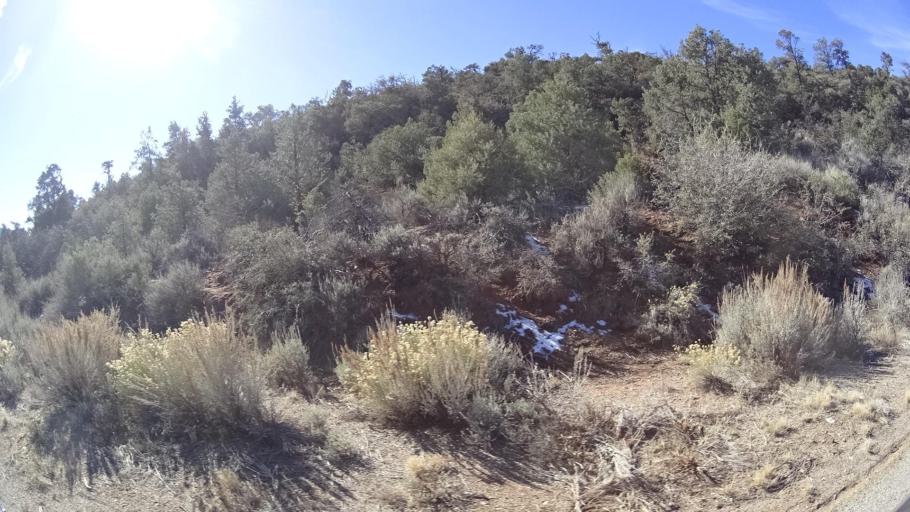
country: US
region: California
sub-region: Kern County
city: Pine Mountain Club
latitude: 34.8676
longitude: -119.2596
